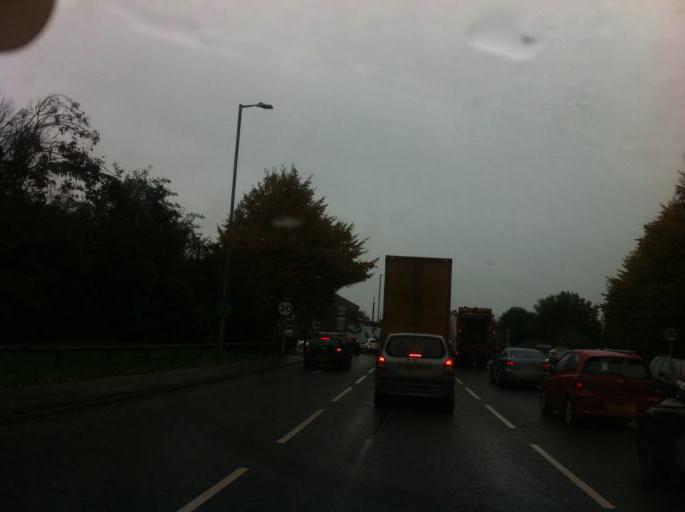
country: GB
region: England
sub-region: Lincolnshire
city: Boston
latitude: 52.9734
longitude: -0.0283
